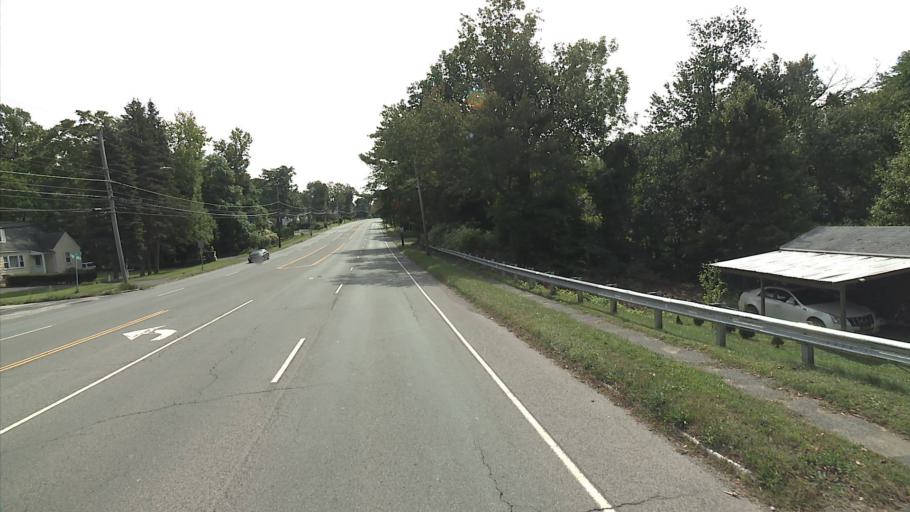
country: US
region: Connecticut
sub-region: Fairfield County
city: North Stamford
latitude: 41.0960
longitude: -73.5478
